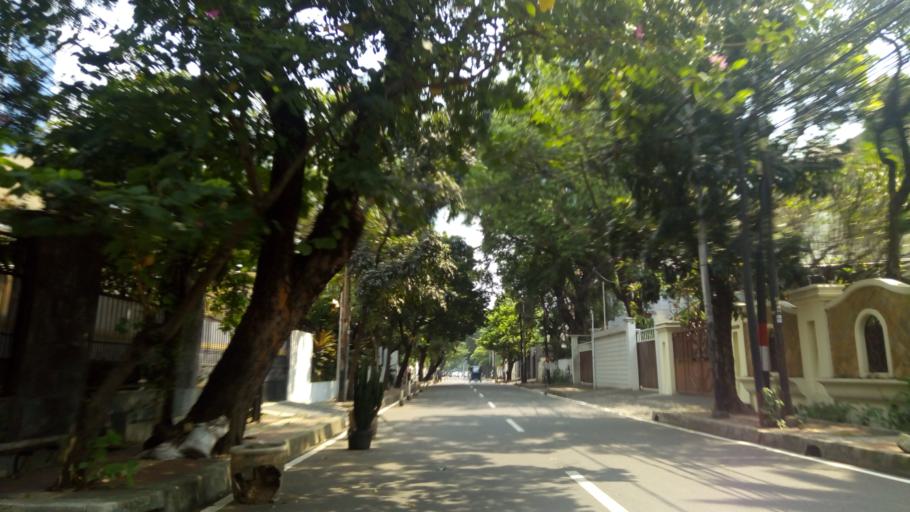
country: ID
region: Jakarta Raya
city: Jakarta
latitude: -6.1996
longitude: 106.8260
